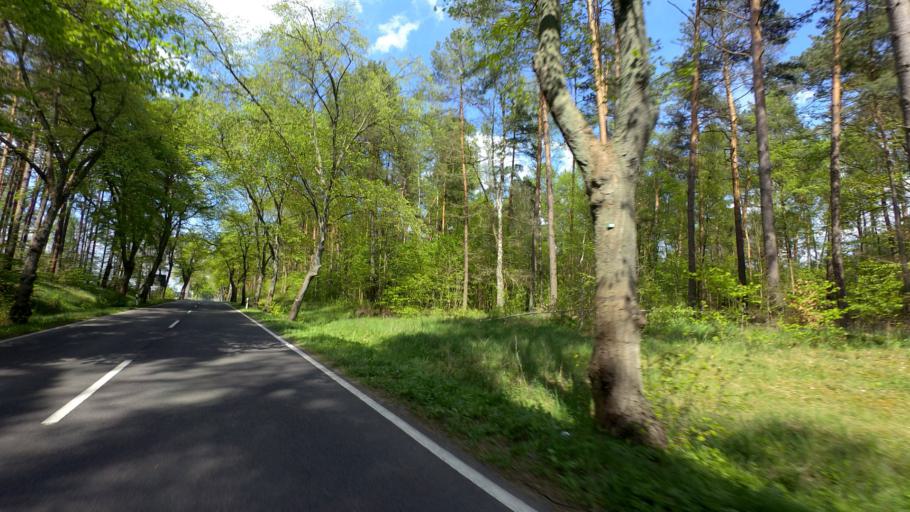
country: DE
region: Brandenburg
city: Milmersdorf
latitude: 53.0610
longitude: 13.6239
